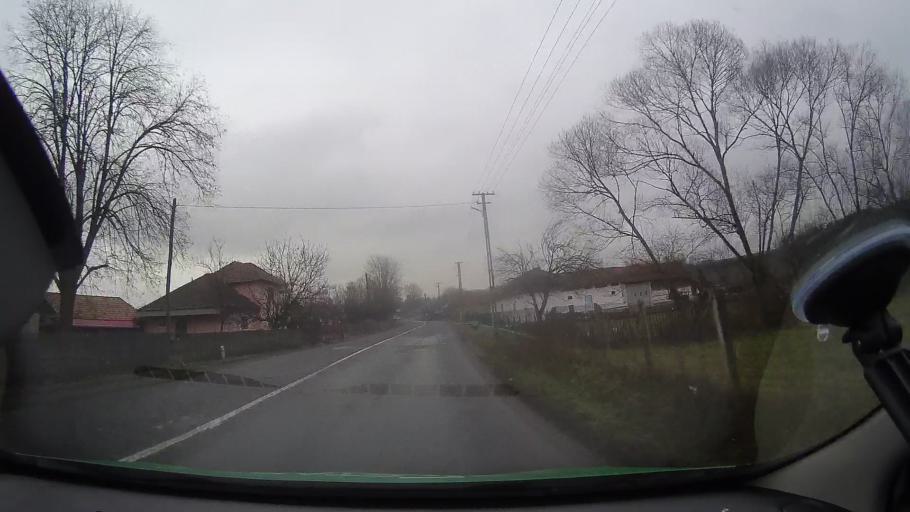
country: RO
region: Arad
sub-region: Comuna Varfurile
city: Varfurile
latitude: 46.3257
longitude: 22.4818
